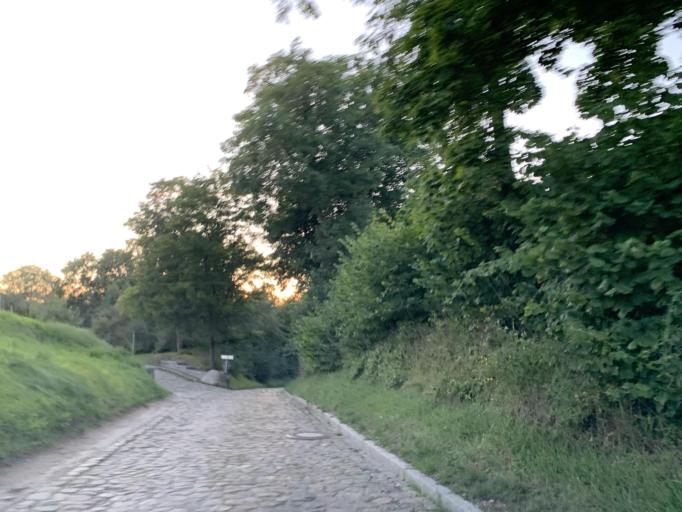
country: DE
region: Mecklenburg-Vorpommern
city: Burg Stargard
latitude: 53.4912
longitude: 13.3062
